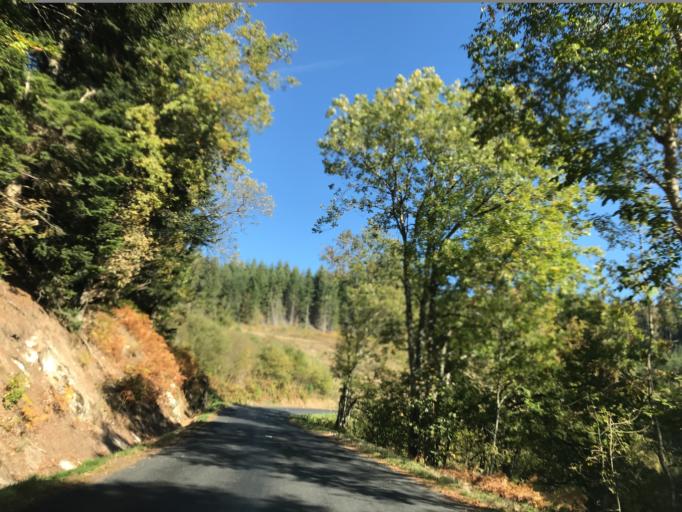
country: FR
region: Auvergne
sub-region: Departement du Puy-de-Dome
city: Celles-sur-Durolle
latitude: 45.7890
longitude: 3.6566
